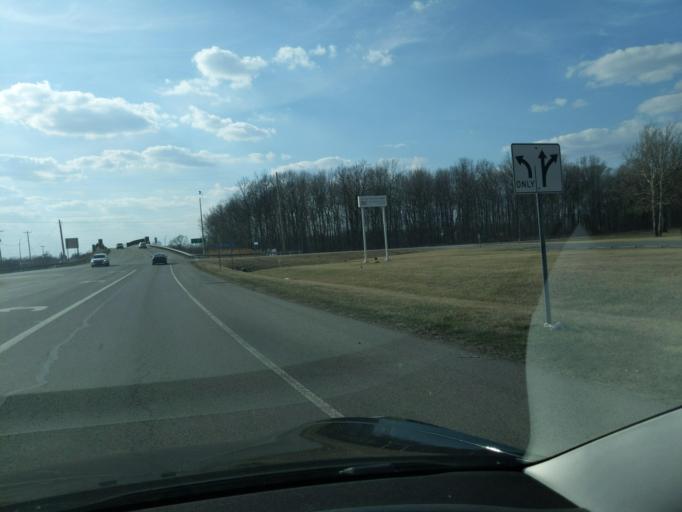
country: US
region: Ohio
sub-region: Allen County
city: Lima
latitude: 40.7168
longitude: -84.0722
